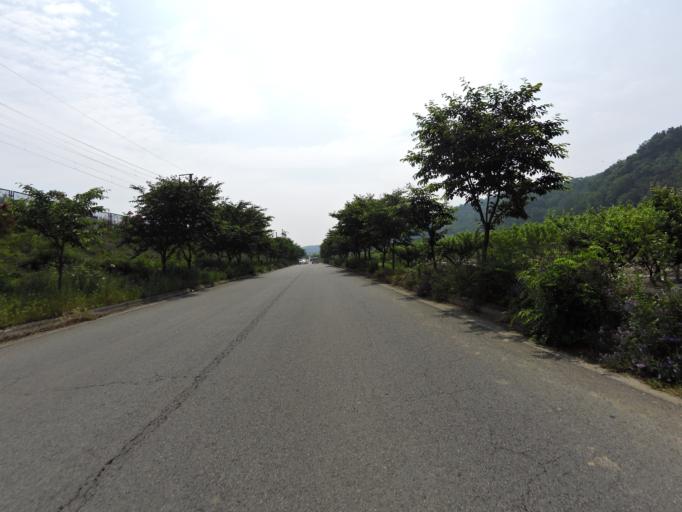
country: KR
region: Gyeongsangbuk-do
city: Gyeongsan-si
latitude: 35.8524
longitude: 128.6984
